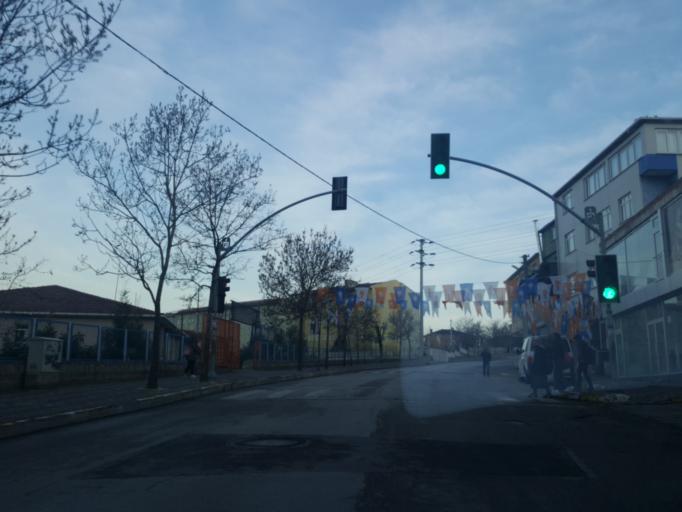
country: TR
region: Kocaeli
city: Tavsancil
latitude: 40.7875
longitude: 29.5390
